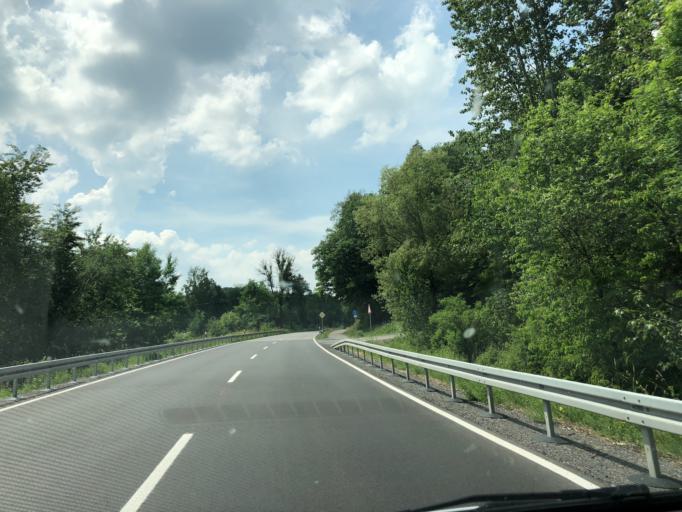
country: DE
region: Hesse
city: Neustadt (Hessen)
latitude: 50.8934
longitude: 9.1572
